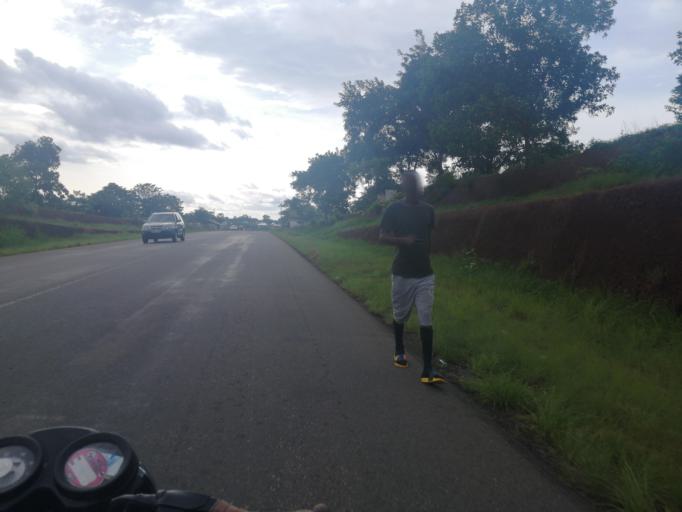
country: SL
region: Northern Province
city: Port Loko
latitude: 8.7713
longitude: -12.7740
